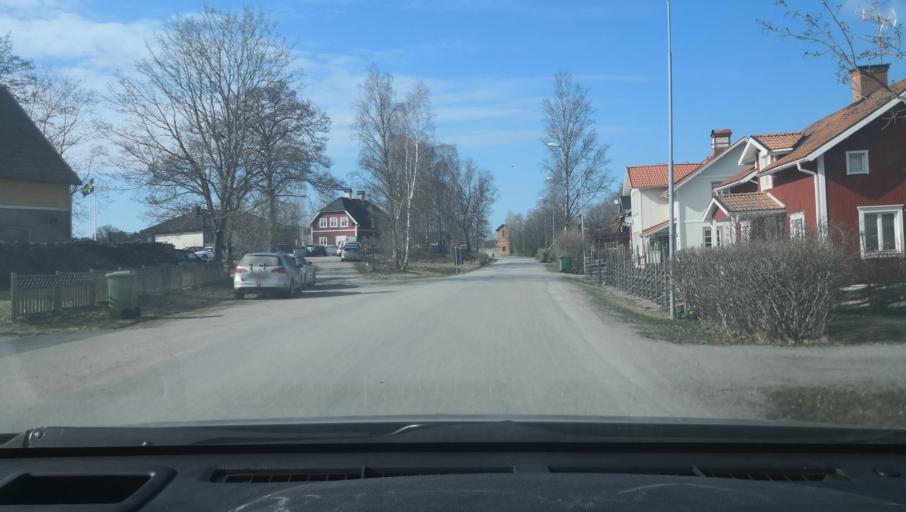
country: SE
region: Uppsala
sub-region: Heby Kommun
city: Morgongava
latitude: 59.8413
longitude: 16.9163
